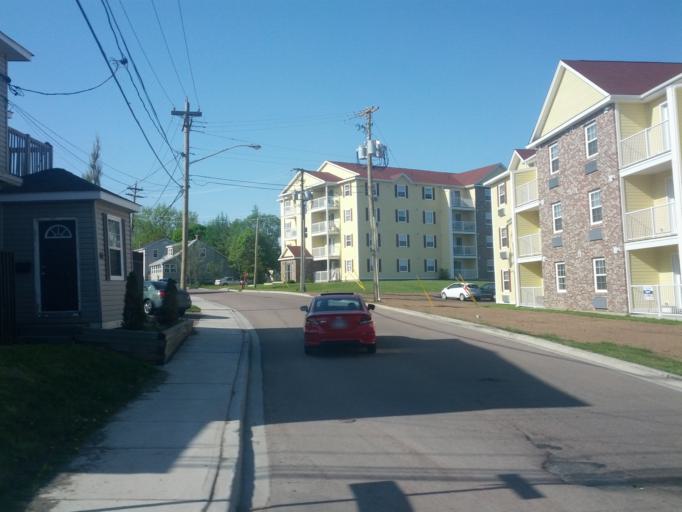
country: CA
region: New Brunswick
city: Moncton
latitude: 46.1025
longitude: -64.7669
